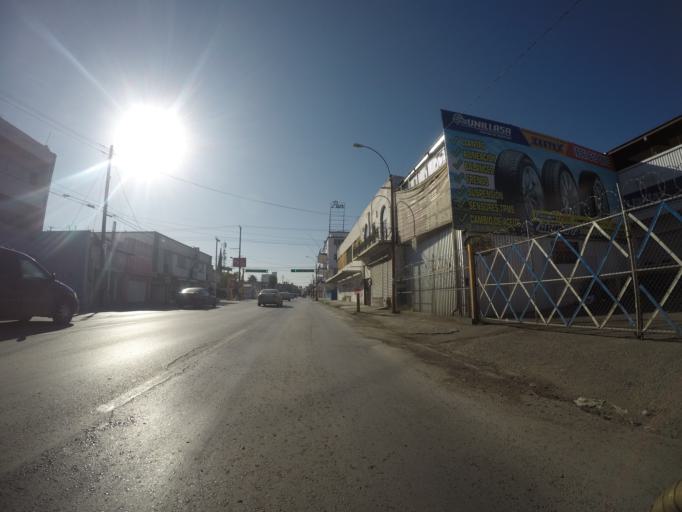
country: MX
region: Chihuahua
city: Ciudad Juarez
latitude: 31.7386
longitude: -106.4733
